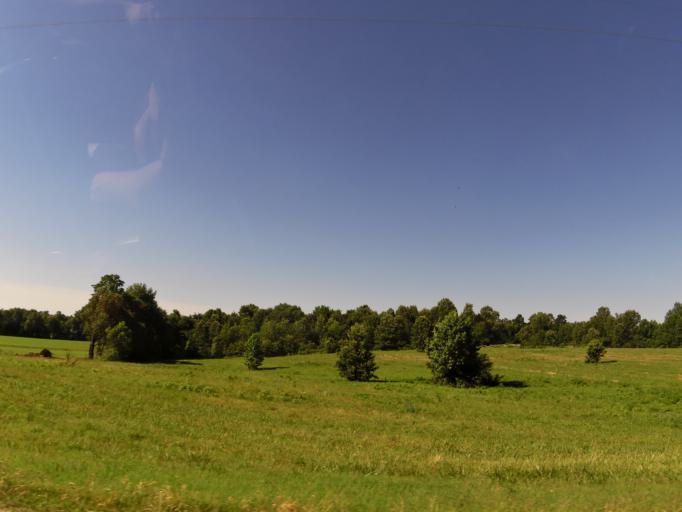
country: US
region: Arkansas
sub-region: Clay County
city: Piggott
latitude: 36.4319
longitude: -90.2986
